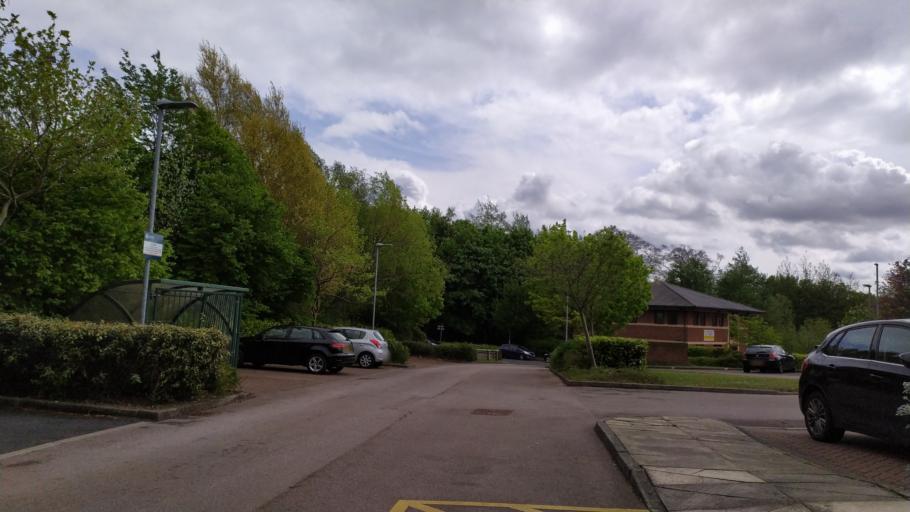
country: GB
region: England
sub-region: City and Borough of Leeds
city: Shadwell
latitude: 53.8056
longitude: -1.4808
